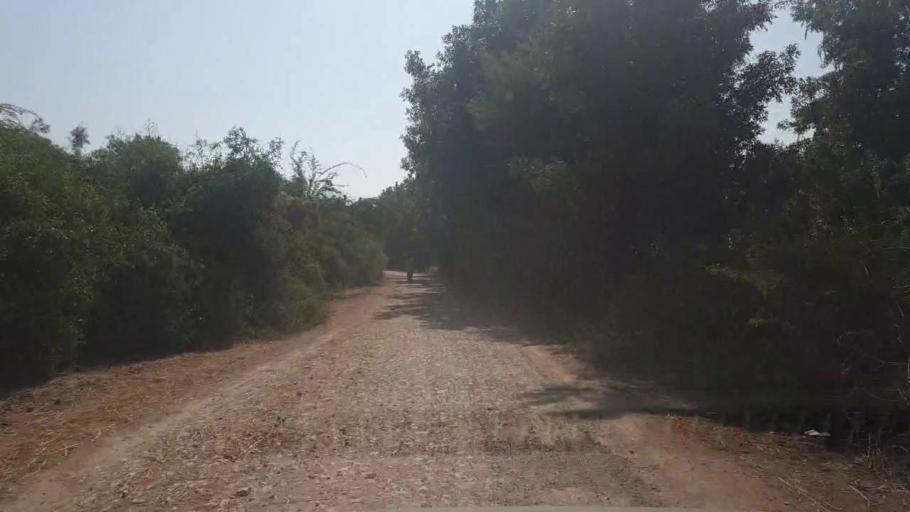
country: PK
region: Sindh
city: Badin
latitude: 24.6763
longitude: 68.8808
